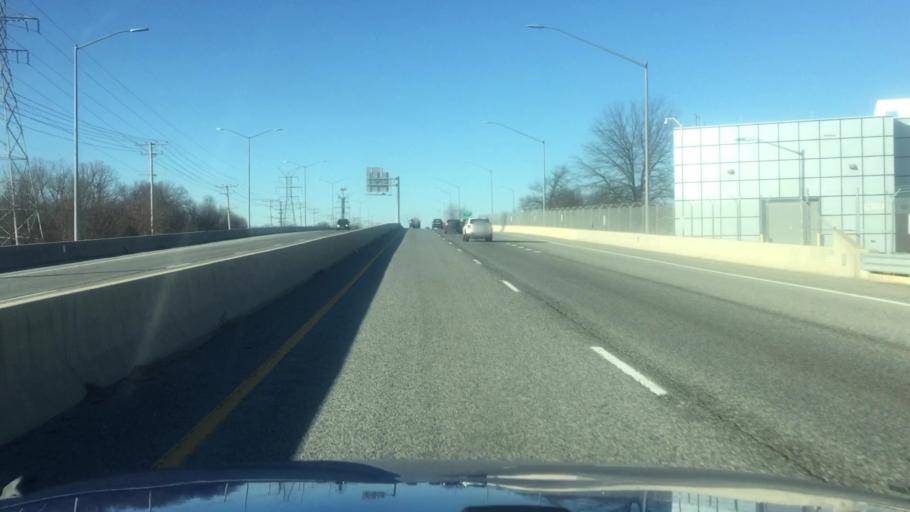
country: US
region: Maryland
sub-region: Howard County
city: Fort George G Mead Junction
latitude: 39.1068
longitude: -76.7735
